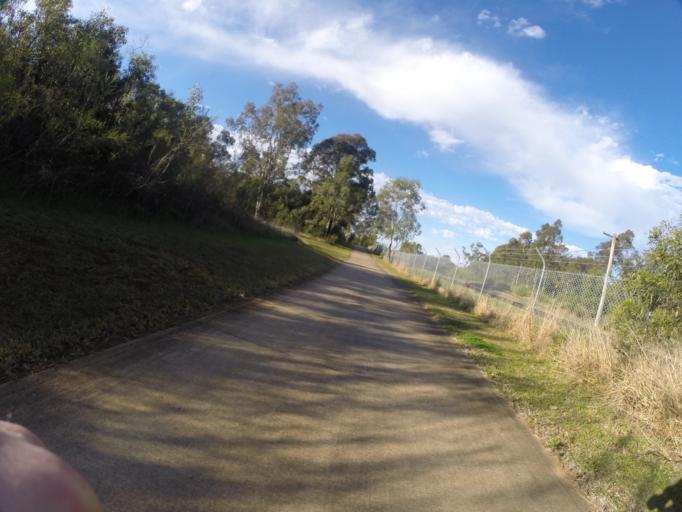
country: AU
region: New South Wales
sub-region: Fairfield
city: Horsley Park
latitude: -33.8486
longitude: 150.8684
